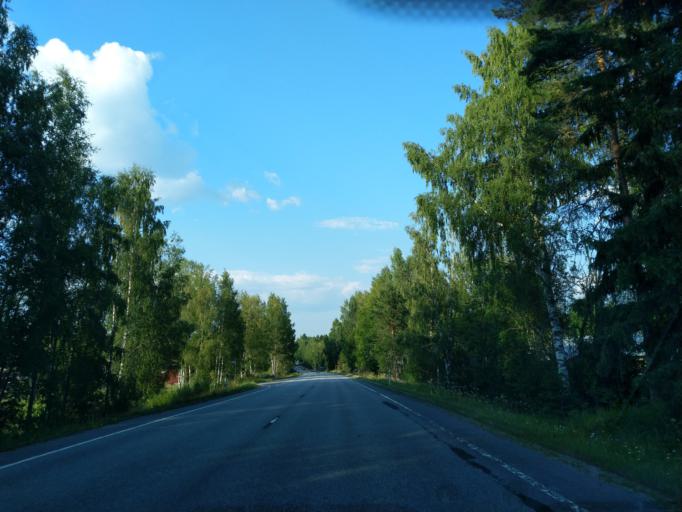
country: FI
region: Satakunta
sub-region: Pori
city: Laengelmaeki
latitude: 61.7551
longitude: 22.1289
